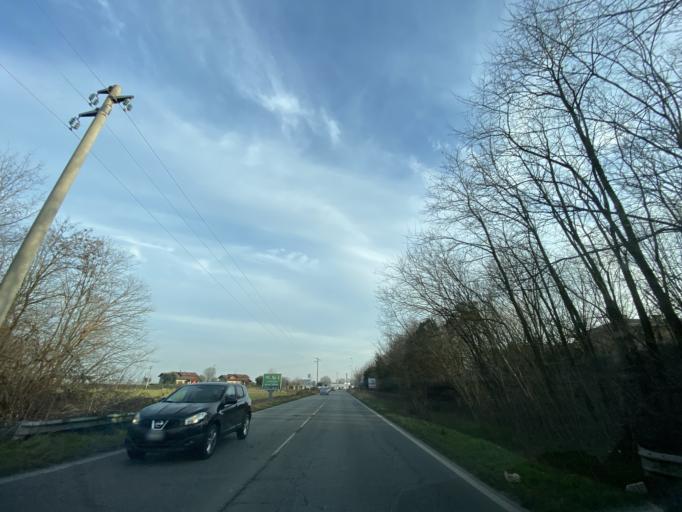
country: IT
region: Lombardy
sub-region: Citta metropolitana di Milano
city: Cernusco sul Naviglio
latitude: 45.5327
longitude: 9.3461
